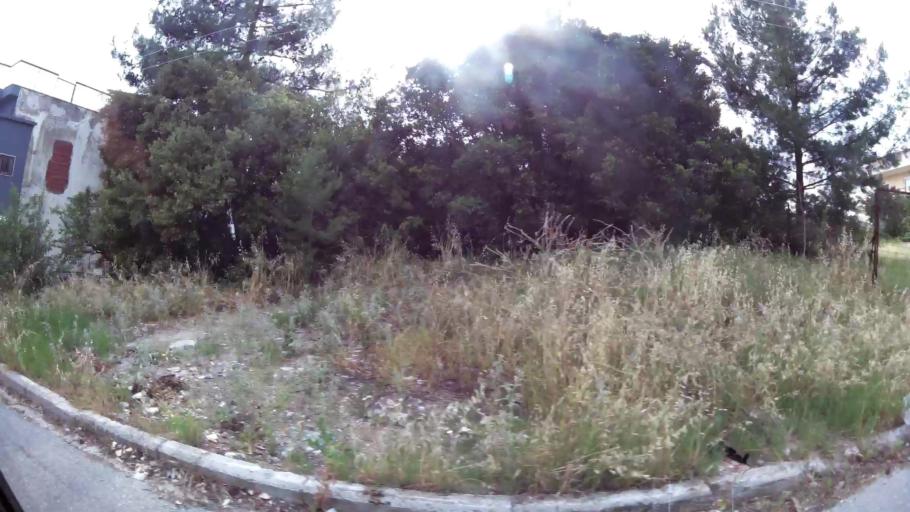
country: GR
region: Central Macedonia
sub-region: Nomos Thessalonikis
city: Oraiokastro
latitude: 40.7310
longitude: 22.9126
